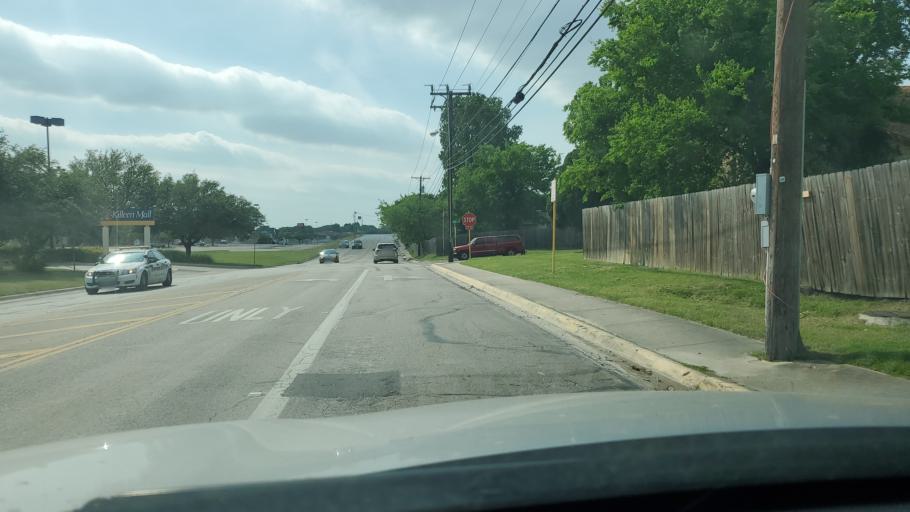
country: US
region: Texas
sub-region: Bell County
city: Killeen
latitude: 31.0937
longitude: -97.7135
